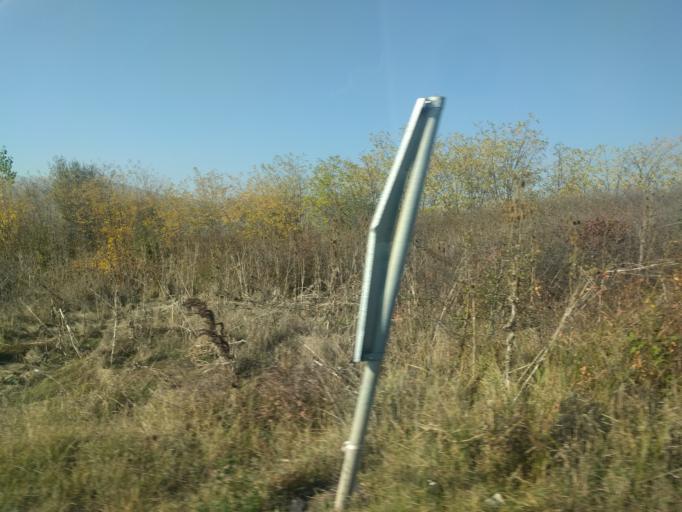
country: XK
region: Pristina
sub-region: Komuna e Gracanices
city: Glanica
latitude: 42.5889
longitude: 21.0174
